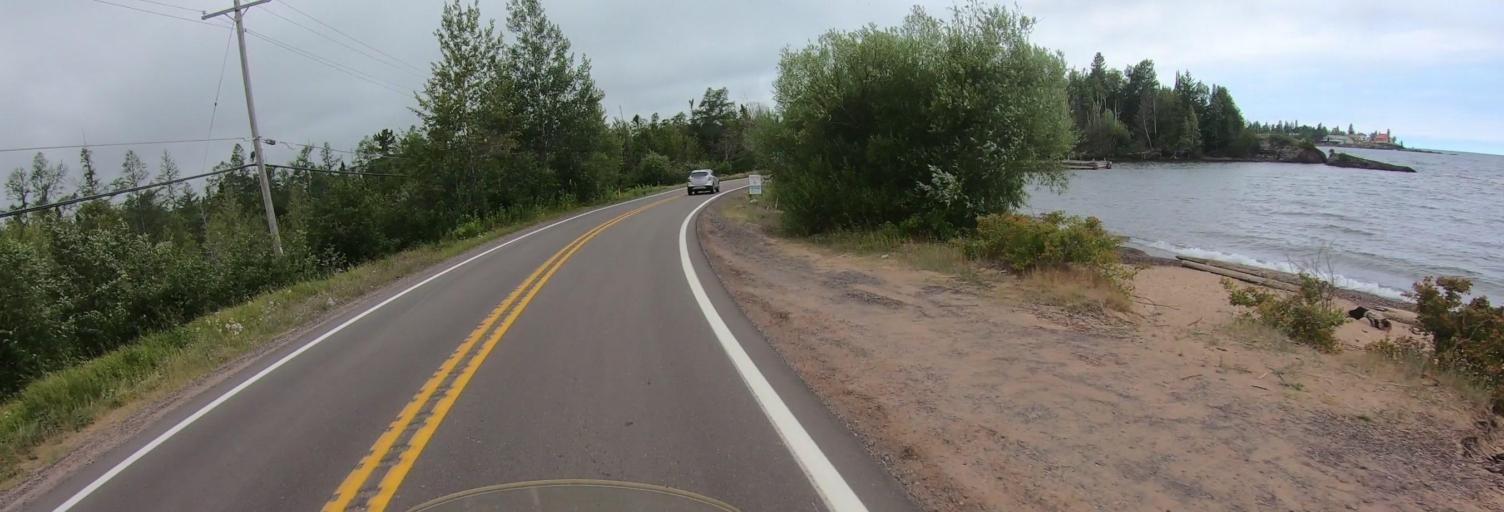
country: US
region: Michigan
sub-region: Keweenaw County
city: Eagle River
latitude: 47.4552
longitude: -88.1505
